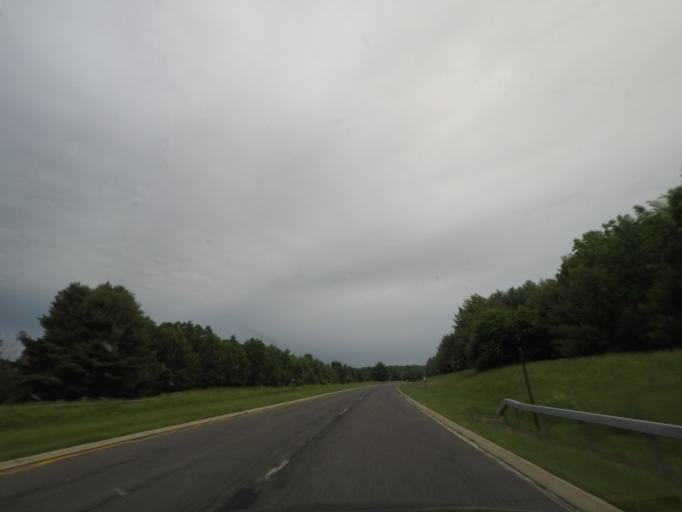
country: US
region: New York
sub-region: Columbia County
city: Chatham
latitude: 42.3927
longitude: -73.5569
